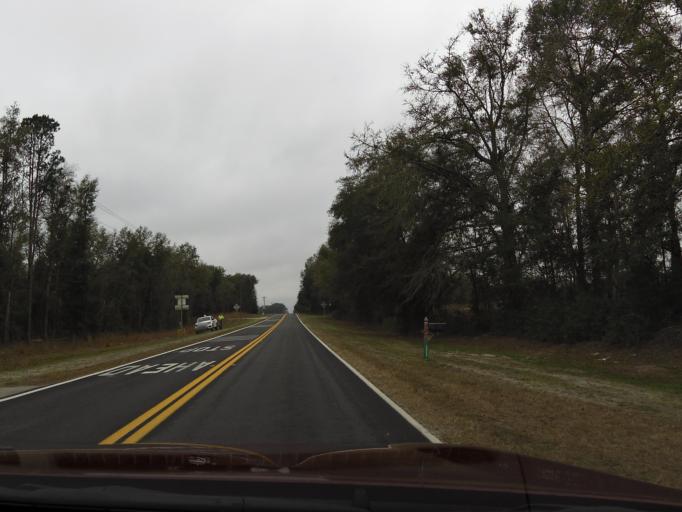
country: US
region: Florida
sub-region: Gilchrist County
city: Trenton
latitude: 29.7961
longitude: -82.8681
